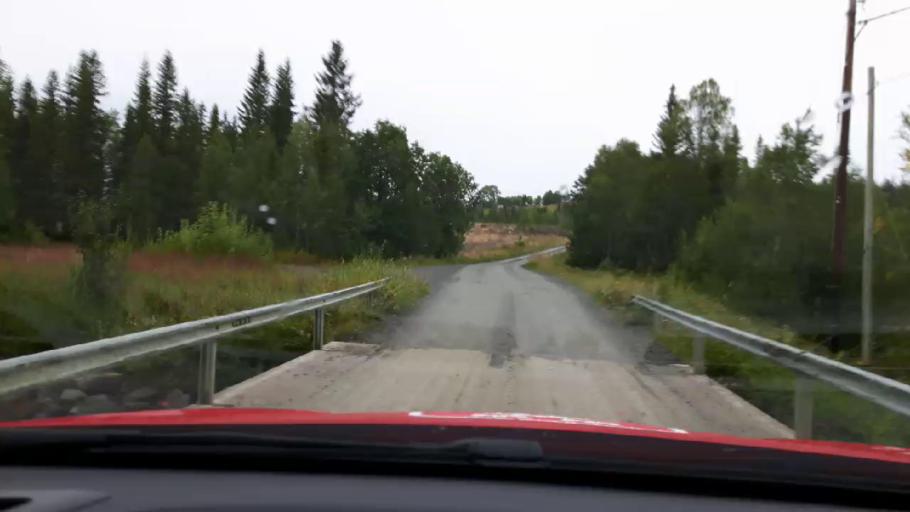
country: SE
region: Jaemtland
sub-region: Are Kommun
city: Are
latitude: 63.5085
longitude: 12.7120
